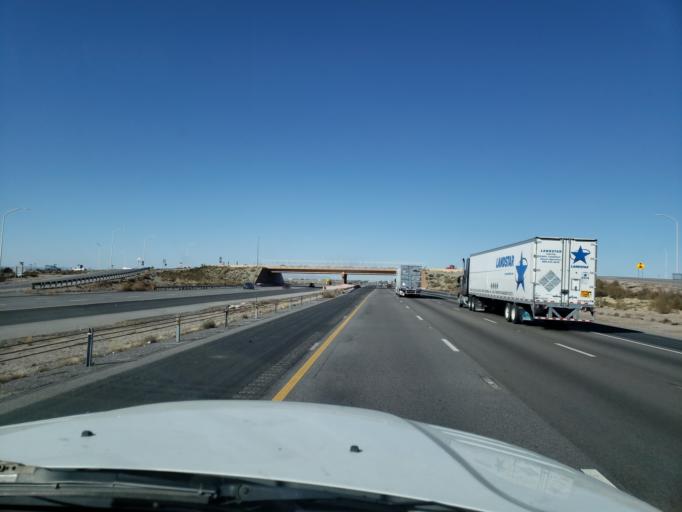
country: US
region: New Mexico
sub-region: Dona Ana County
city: Mesquite
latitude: 32.1726
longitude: -106.6686
